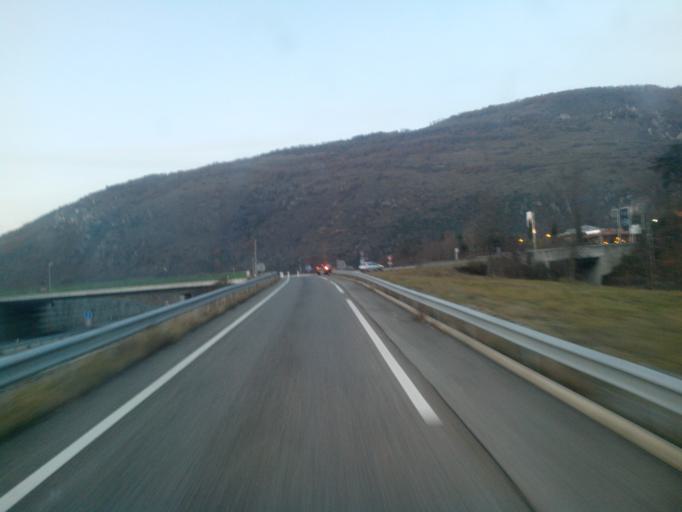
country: FR
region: Midi-Pyrenees
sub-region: Departement de l'Ariege
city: Montgaillard
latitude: 42.9480
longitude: 1.6224
